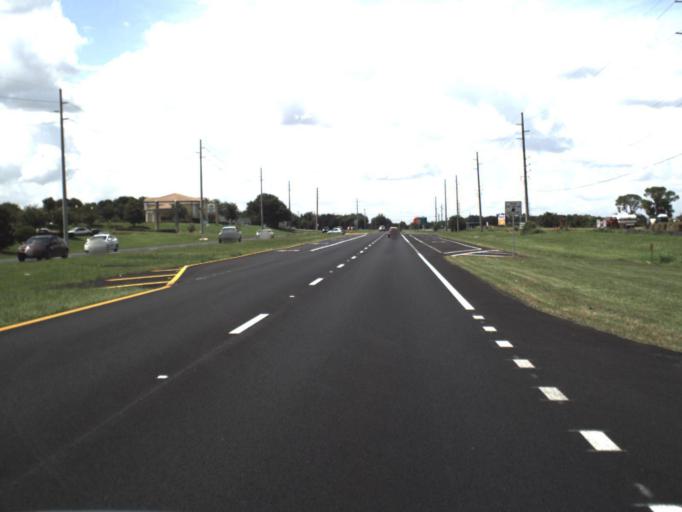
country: US
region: Florida
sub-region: Polk County
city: Cypress Gardens
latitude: 27.9832
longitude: -81.6793
